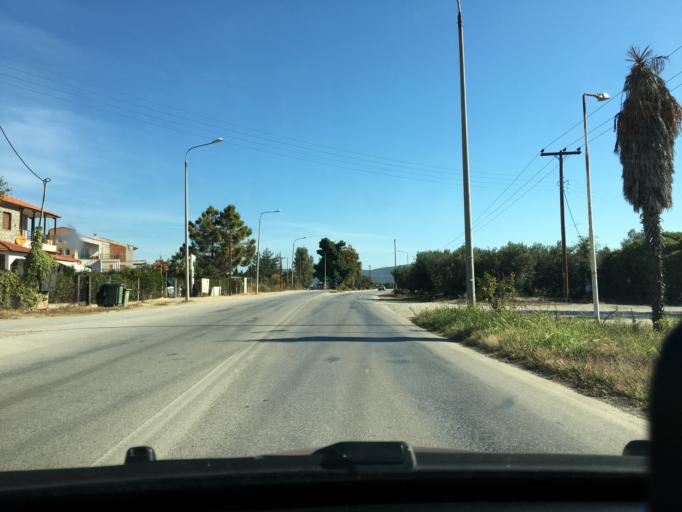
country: GR
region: Central Macedonia
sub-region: Nomos Chalkidikis
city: Ormylia
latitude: 40.2619
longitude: 23.5129
